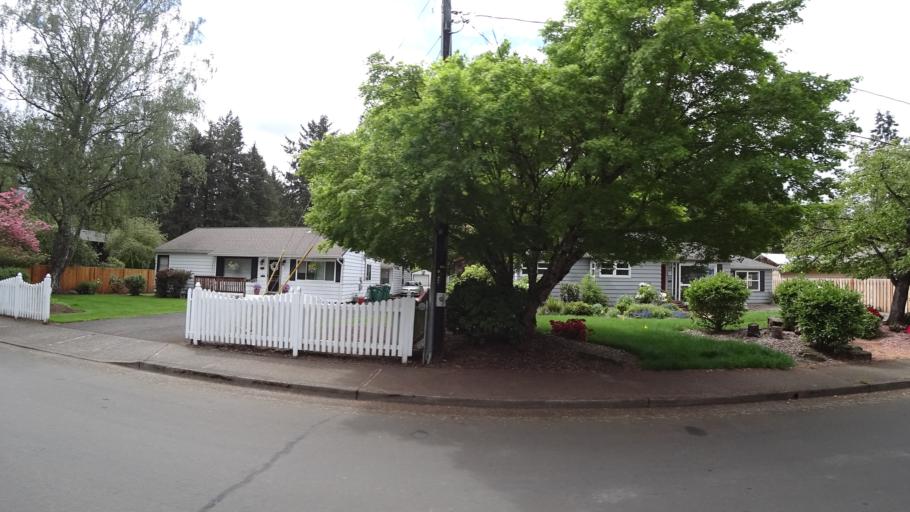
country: US
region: Oregon
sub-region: Washington County
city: Beaverton
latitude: 45.4796
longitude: -122.8334
